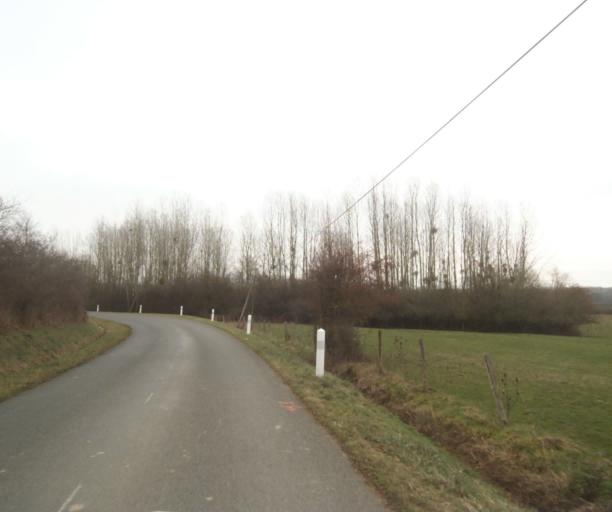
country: FR
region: Champagne-Ardenne
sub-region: Departement de la Marne
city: Pargny-sur-Saulx
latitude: 48.7416
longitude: 4.8393
